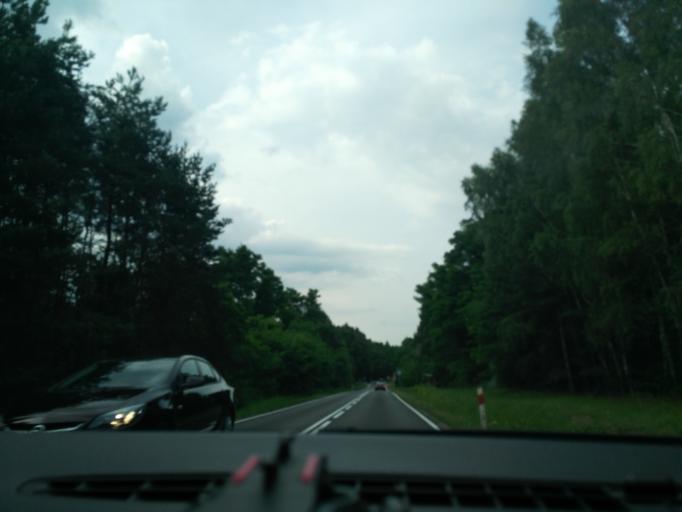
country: PL
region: Subcarpathian Voivodeship
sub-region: Powiat nizanski
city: Jezowe
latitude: 50.4006
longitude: 22.1305
